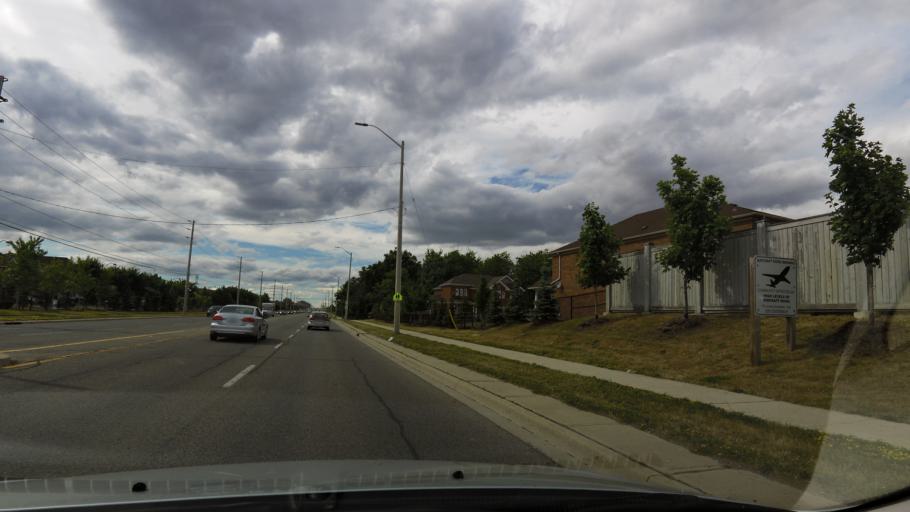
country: CA
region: Ontario
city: Brampton
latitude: 43.6389
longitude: -79.7200
